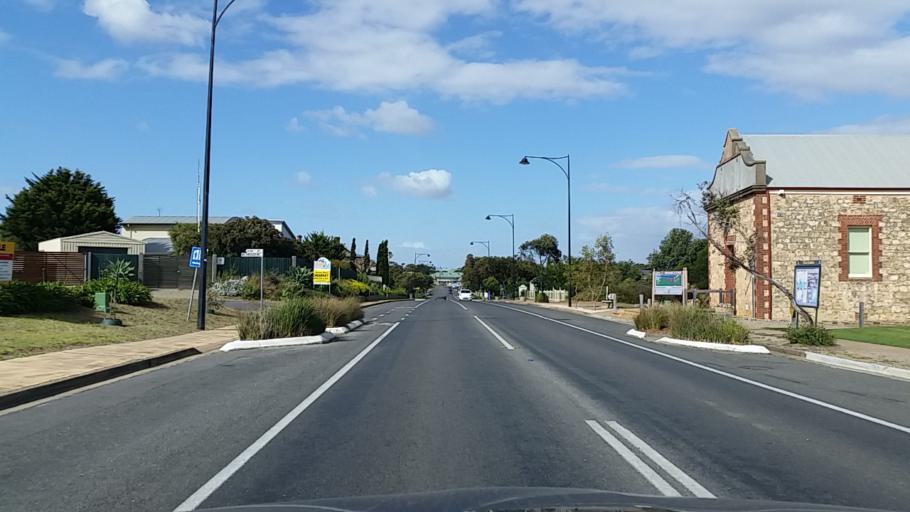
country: AU
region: South Australia
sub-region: Alexandrina
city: Port Elliot
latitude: -35.5100
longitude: 138.7061
